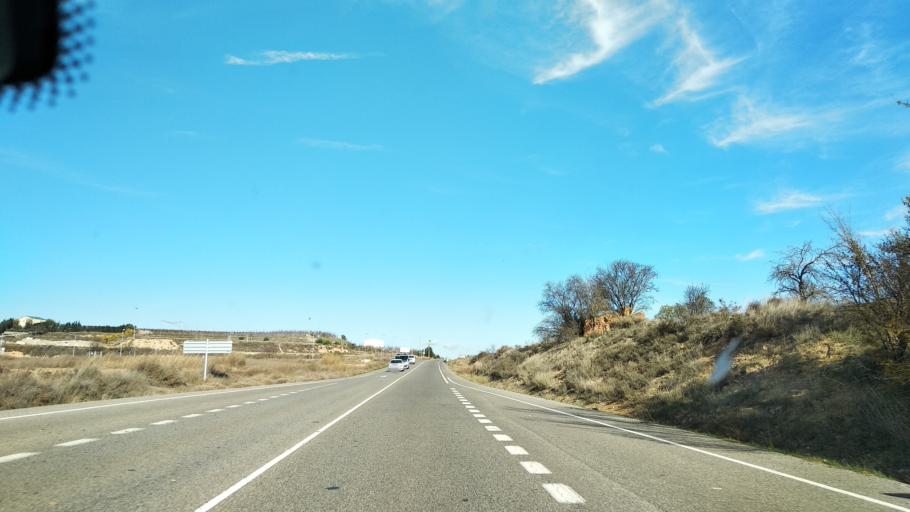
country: ES
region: Catalonia
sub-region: Provincia de Lleida
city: Corbins
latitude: 41.7038
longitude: 0.7105
